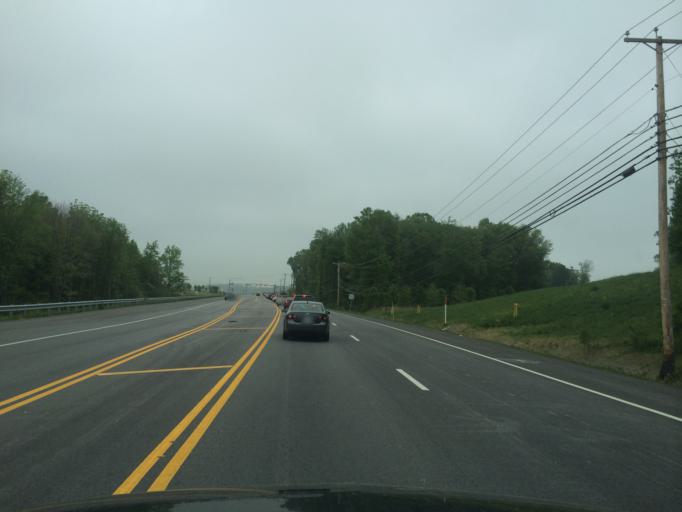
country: US
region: Maryland
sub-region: Carroll County
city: Sykesville
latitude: 39.3132
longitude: -76.8985
